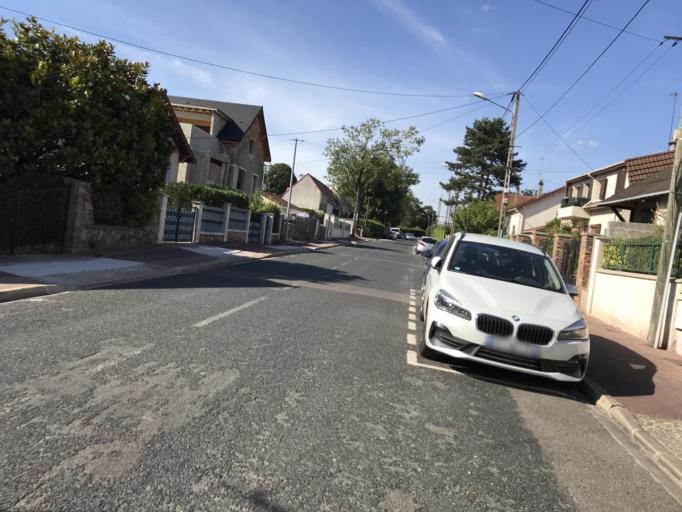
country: FR
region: Ile-de-France
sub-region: Departement de l'Essonne
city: Saint-Michel-sur-Orge
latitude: 48.6438
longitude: 2.3048
